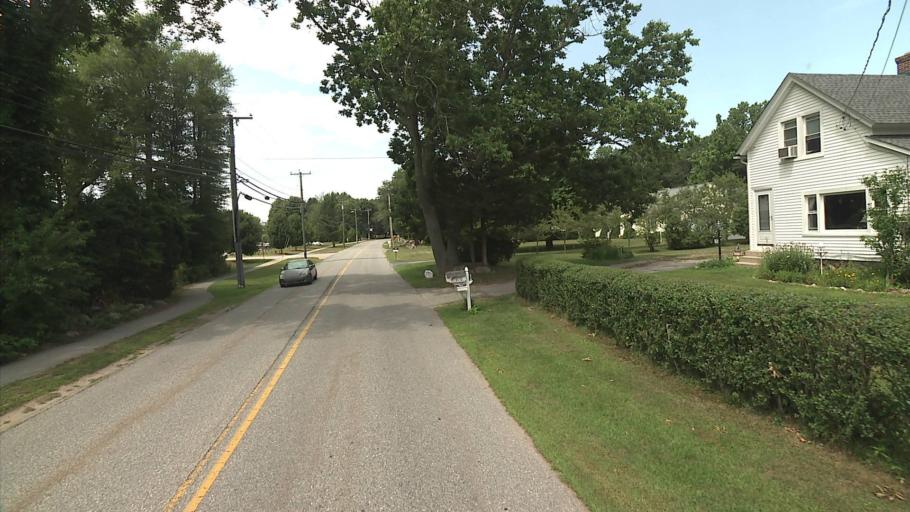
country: US
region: Connecticut
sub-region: New London County
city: Central Waterford
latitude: 41.3128
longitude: -72.1317
